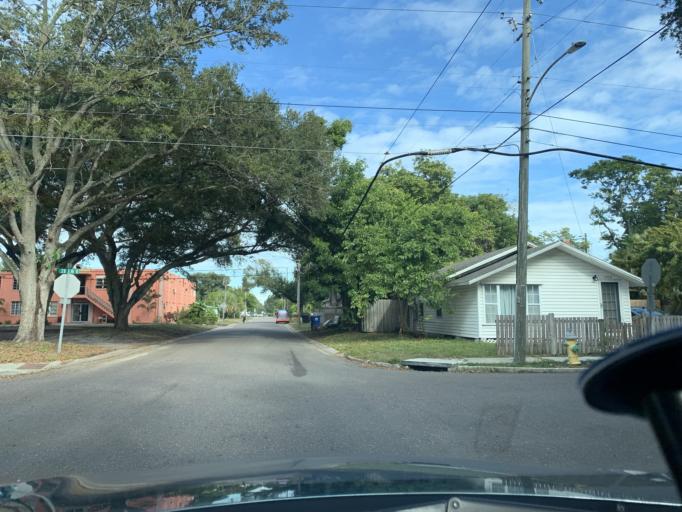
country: US
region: Florida
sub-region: Pinellas County
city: Lealman
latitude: 27.7974
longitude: -82.6581
